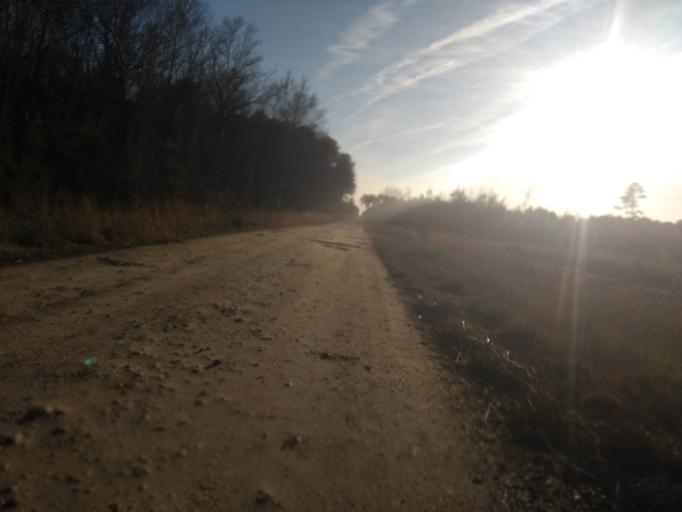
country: FR
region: Aquitaine
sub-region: Departement de la Gironde
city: Le Barp
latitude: 44.6011
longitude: -0.7965
